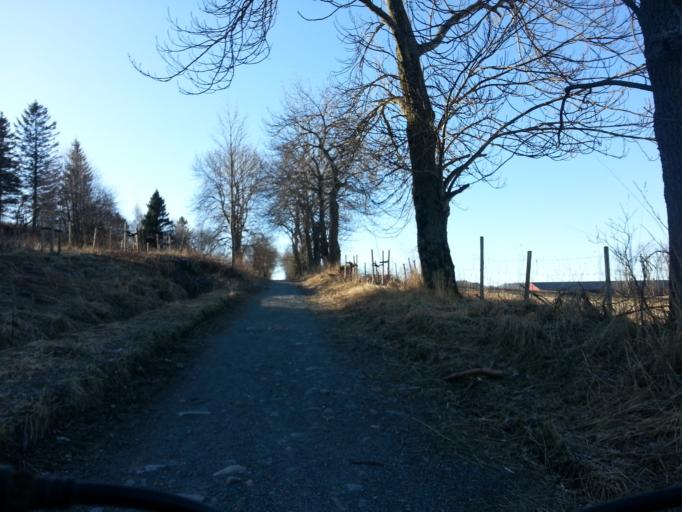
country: NO
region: Sor-Trondelag
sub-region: Trondheim
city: Trondheim
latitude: 63.4342
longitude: 10.4837
